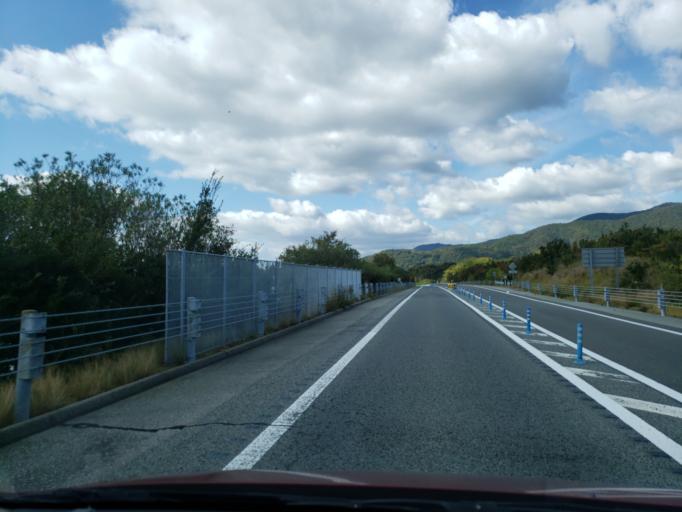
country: JP
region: Tokushima
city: Kamojimacho-jogejima
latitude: 34.1217
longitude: 134.3674
